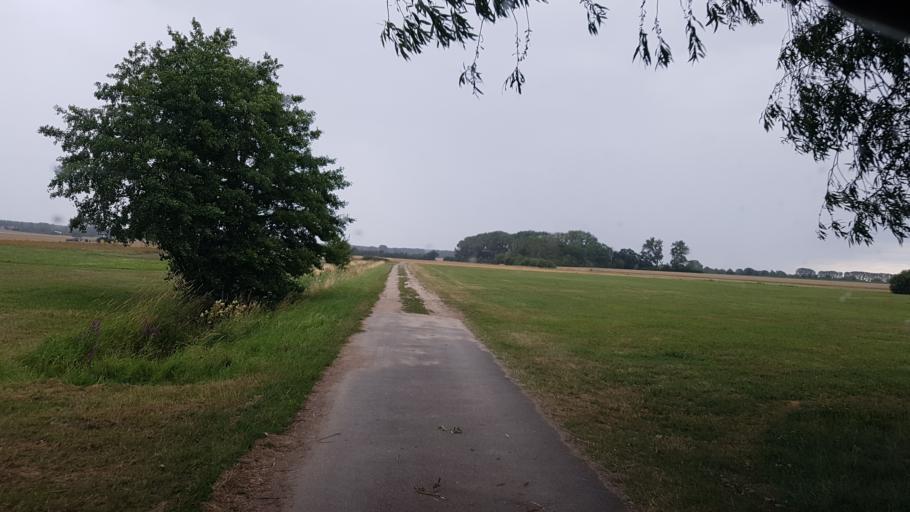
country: DE
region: Brandenburg
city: Sonnewalde
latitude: 51.7041
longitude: 13.6980
